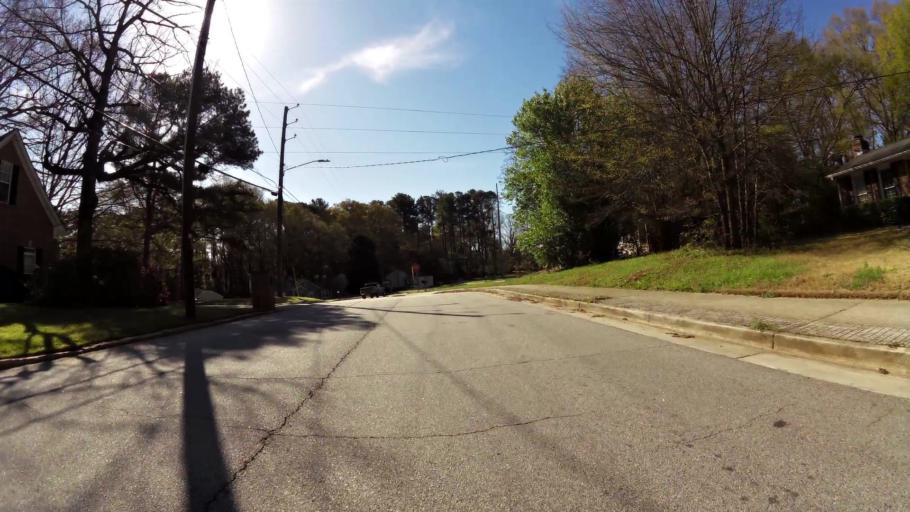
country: US
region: Georgia
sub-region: DeKalb County
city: Clarkston
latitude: 33.8257
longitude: -84.2664
